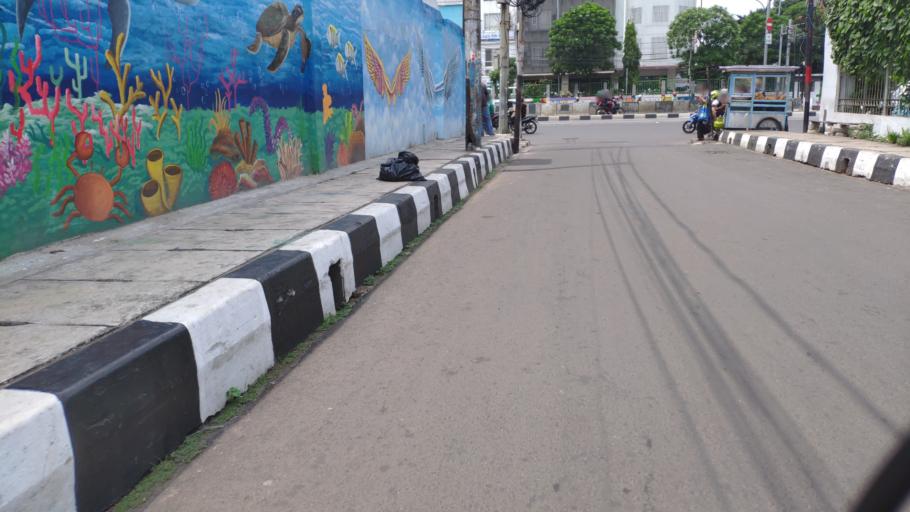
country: ID
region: Jakarta Raya
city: Jakarta
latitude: -6.2109
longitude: 106.8606
